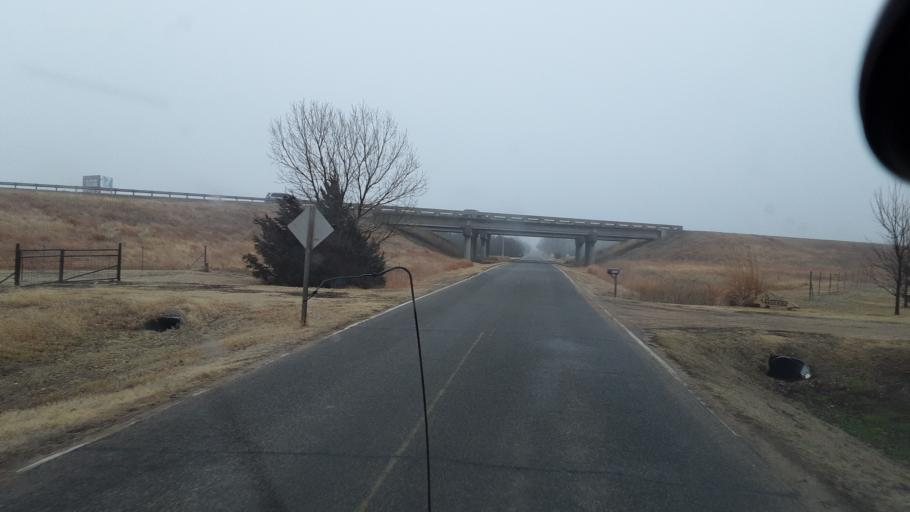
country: US
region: Kansas
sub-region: Reno County
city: South Hutchinson
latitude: 37.9410
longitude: -97.8830
